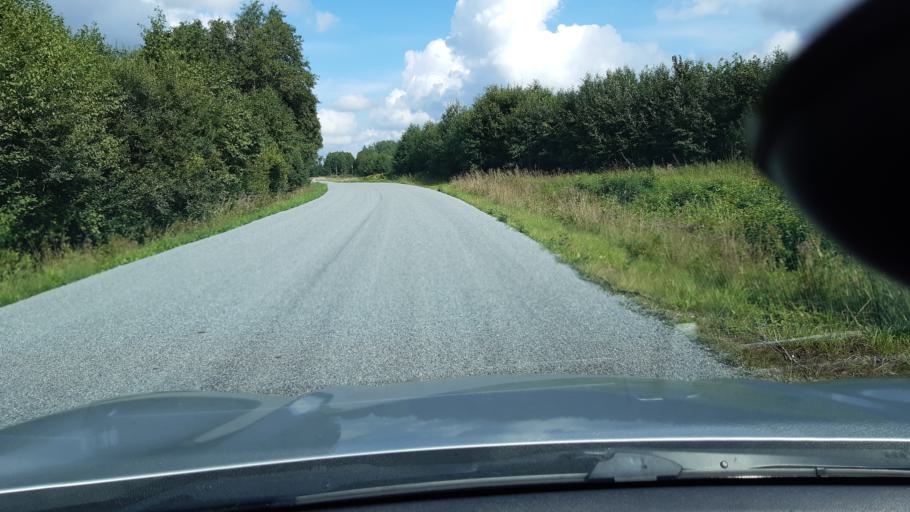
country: EE
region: Raplamaa
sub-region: Kehtna vald
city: Kehtna
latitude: 58.9062
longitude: 25.1008
